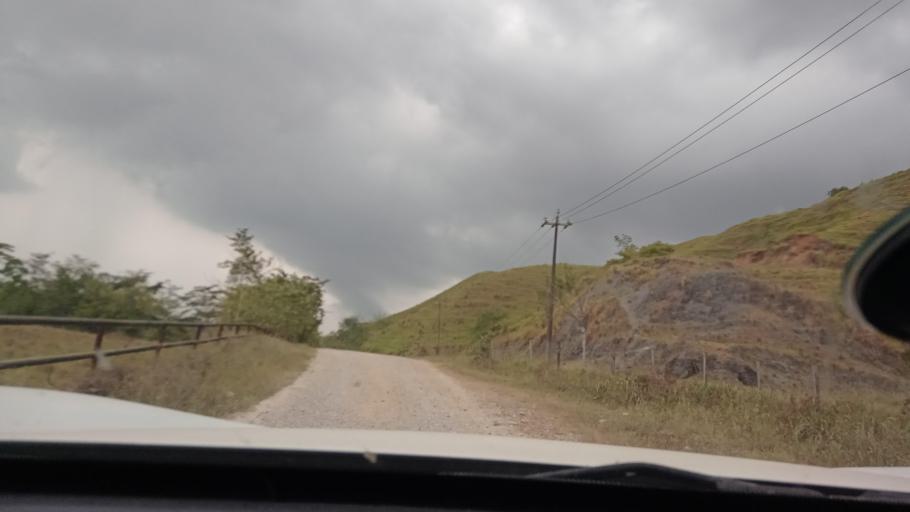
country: MX
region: Tabasco
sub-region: Huimanguillo
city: Francisco Rueda
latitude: 17.4387
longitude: -94.0612
